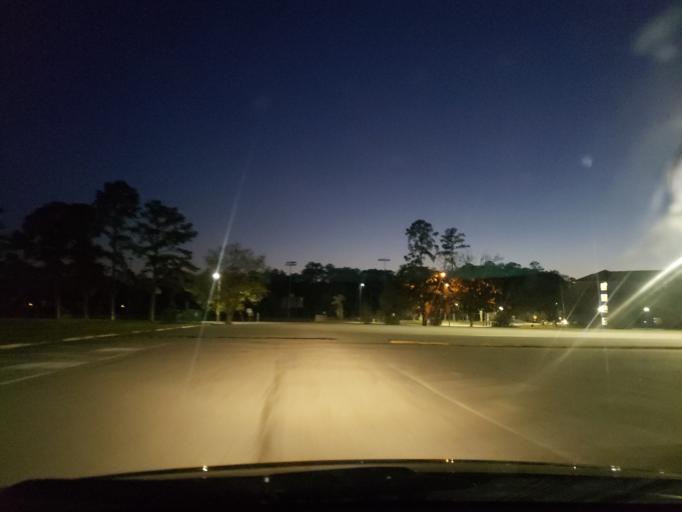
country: US
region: Georgia
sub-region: Chatham County
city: Montgomery
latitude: 31.9770
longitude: -81.1614
